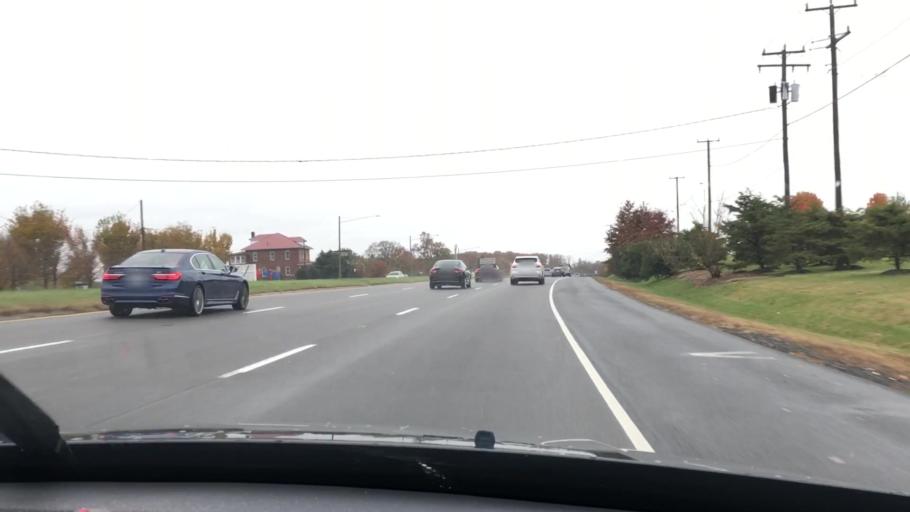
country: US
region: Virginia
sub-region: Fairfax County
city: Lorton
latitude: 38.6981
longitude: -77.2564
